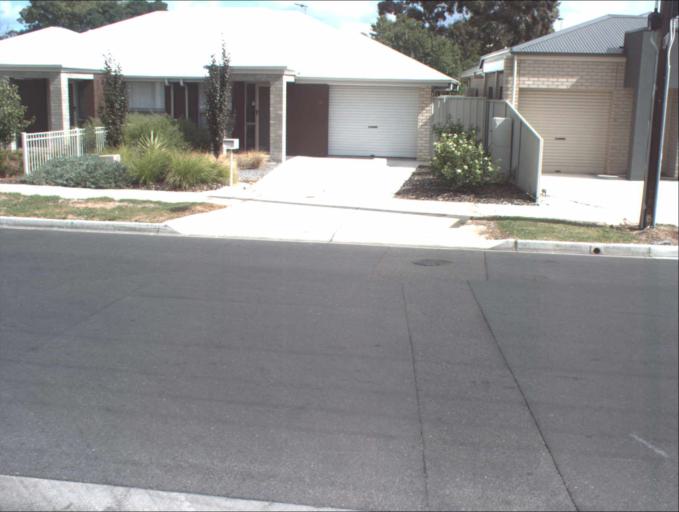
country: AU
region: South Australia
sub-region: Port Adelaide Enfield
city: Blair Athol
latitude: -34.8607
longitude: 138.5953
